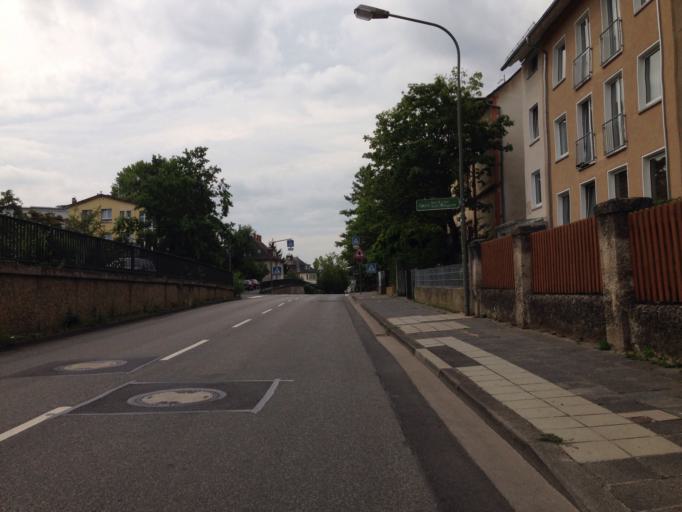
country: DE
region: Hesse
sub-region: Regierungsbezirk Giessen
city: Giessen
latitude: 50.5819
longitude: 8.6841
